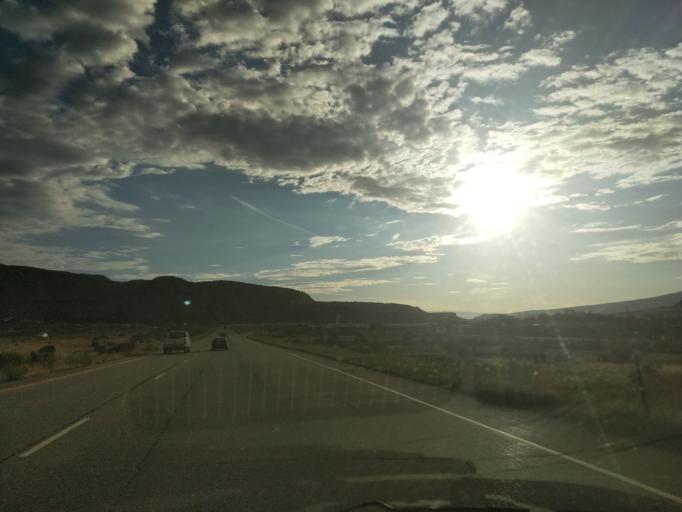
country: US
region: Colorado
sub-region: Garfield County
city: Battlement Mesa
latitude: 39.4943
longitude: -107.9462
